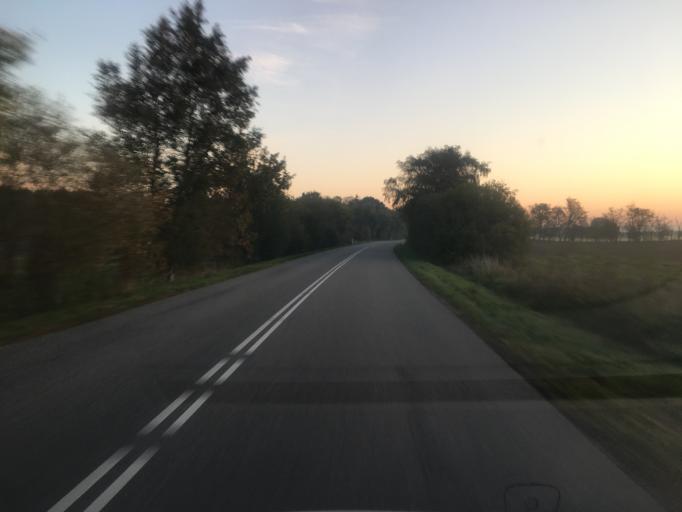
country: DE
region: Schleswig-Holstein
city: Bramstedtlund
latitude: 54.9692
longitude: 9.1220
